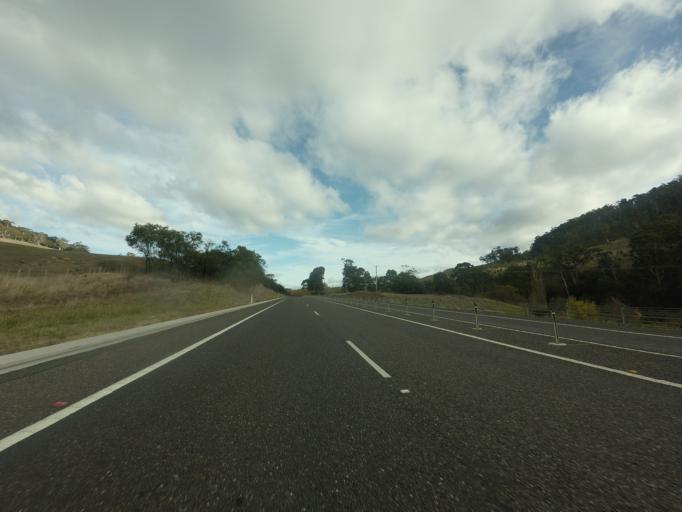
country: AU
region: Tasmania
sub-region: Brighton
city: Bridgewater
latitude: -42.5554
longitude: 147.2099
